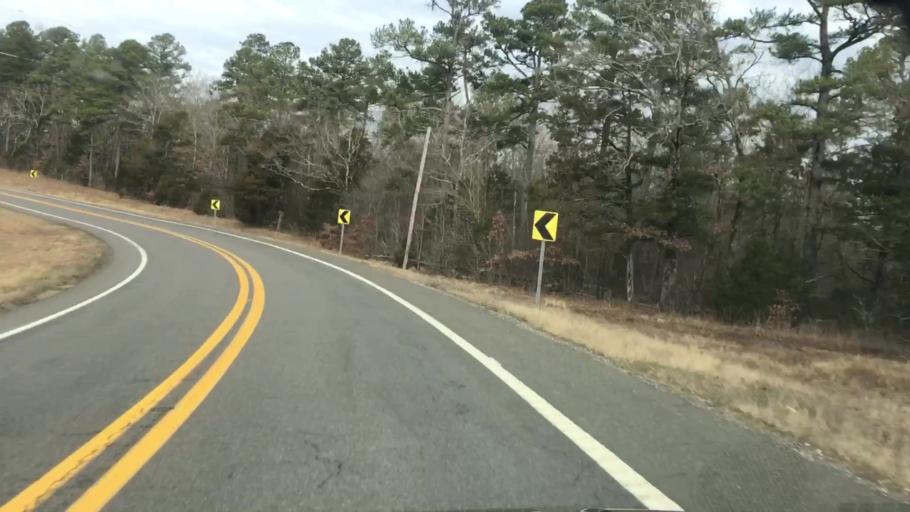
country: US
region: Arkansas
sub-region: Montgomery County
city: Mount Ida
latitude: 34.6195
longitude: -93.7043
